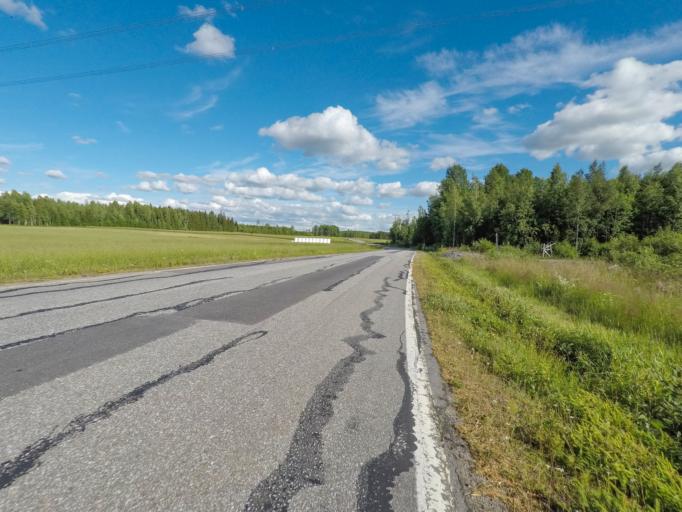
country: FI
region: South Karelia
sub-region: Imatra
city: Imatra
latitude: 61.1381
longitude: 28.6494
